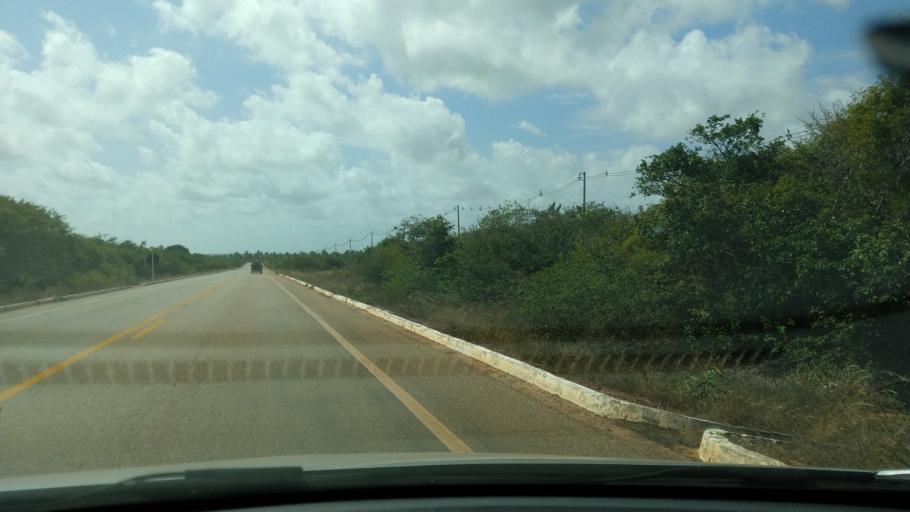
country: BR
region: Rio Grande do Norte
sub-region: Touros
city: Touros
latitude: -5.1974
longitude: -35.5026
